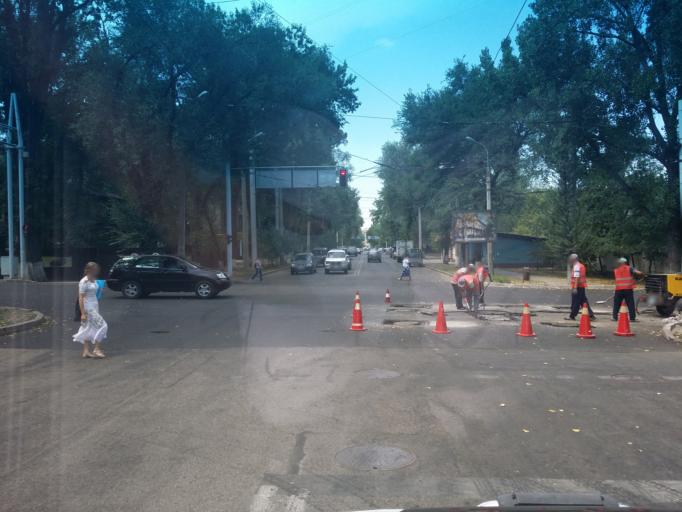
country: KZ
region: Almaty Qalasy
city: Almaty
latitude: 43.2436
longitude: 76.9308
